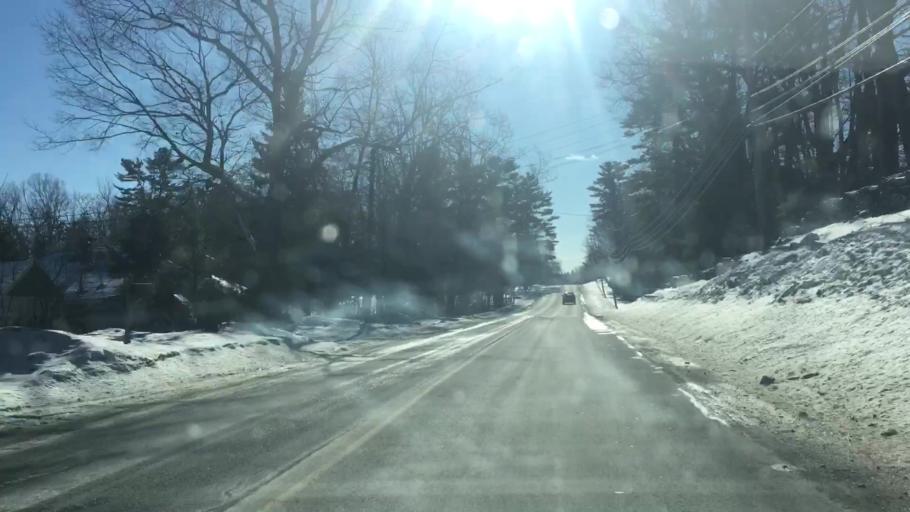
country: US
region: Maine
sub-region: Hancock County
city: Ellsworth
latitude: 44.5367
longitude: -68.4306
